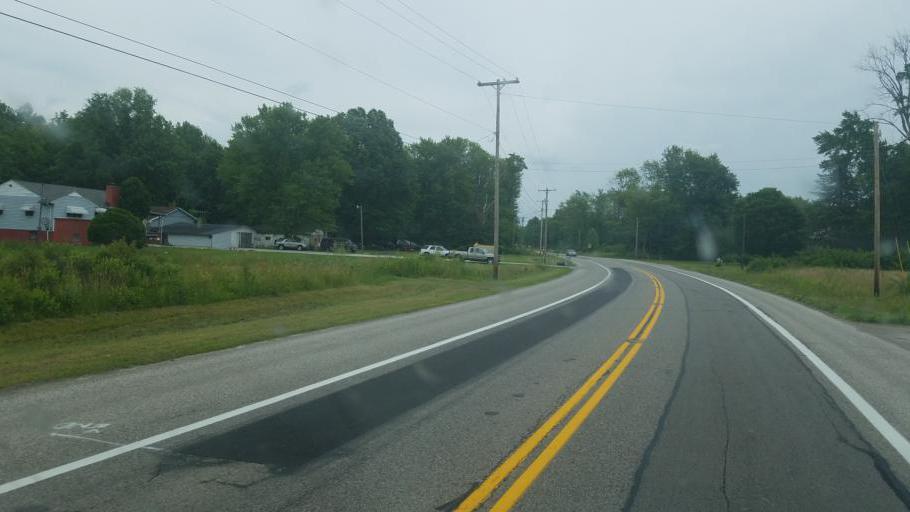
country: US
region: Ohio
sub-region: Ashtabula County
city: Orwell
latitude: 41.4606
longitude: -80.9154
